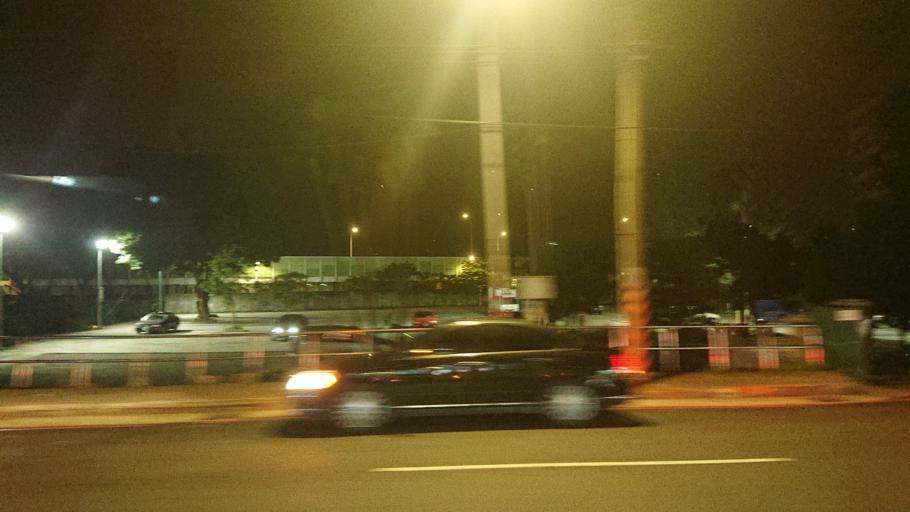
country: TW
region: Taipei
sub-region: Taipei
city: Banqiao
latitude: 24.9532
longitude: 121.4119
